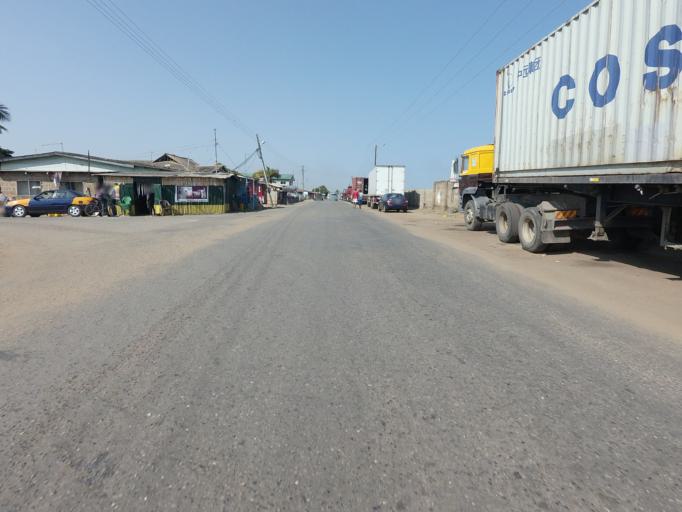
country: GH
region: Greater Accra
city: Teshi Old Town
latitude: 5.5762
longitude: -0.1086
